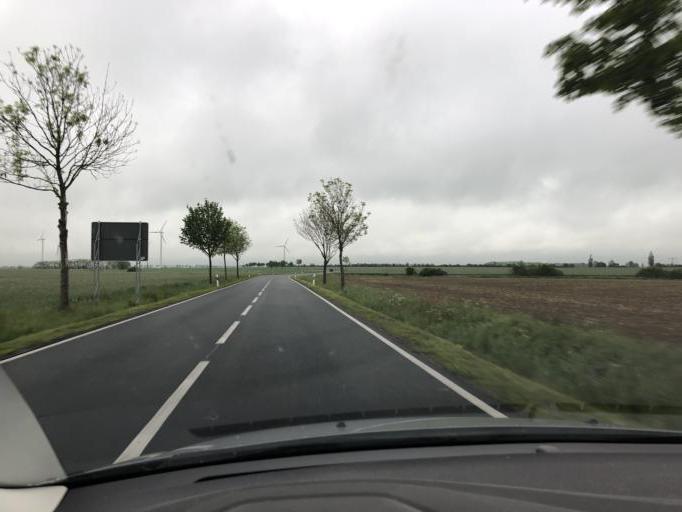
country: DE
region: Saxony
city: Dobernitz
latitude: 51.5120
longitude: 12.3718
